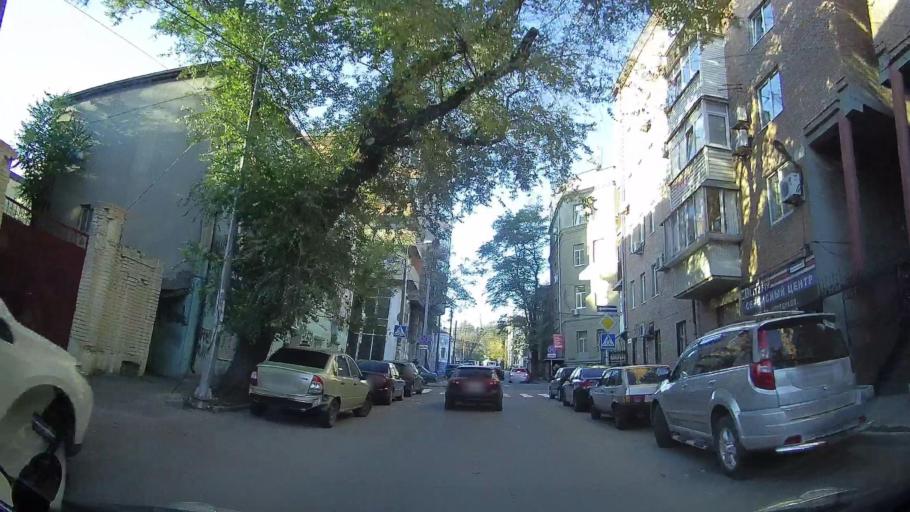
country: RU
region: Rostov
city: Rostov-na-Donu
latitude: 47.2156
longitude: 39.7069
